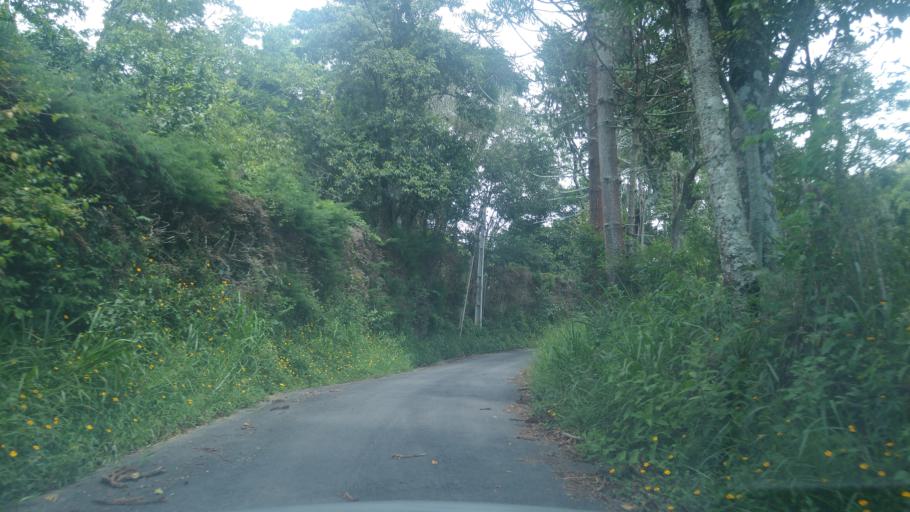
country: BR
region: Minas Gerais
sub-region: Extrema
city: Extrema
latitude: -22.7521
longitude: -46.2932
